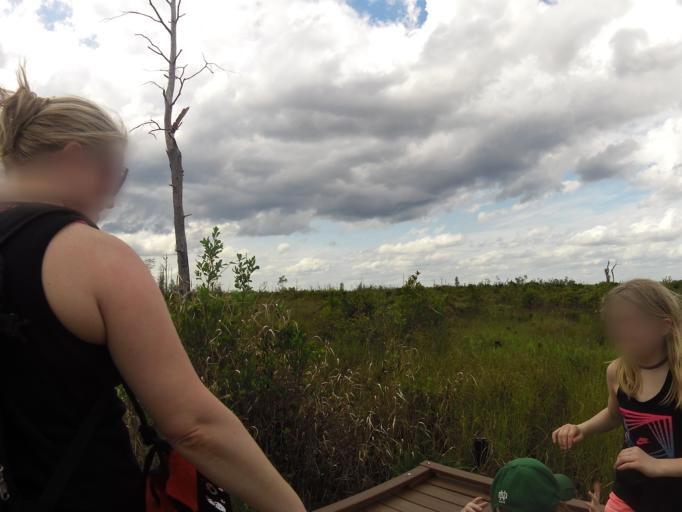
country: US
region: Georgia
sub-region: Charlton County
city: Folkston
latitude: 30.7129
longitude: -82.1663
